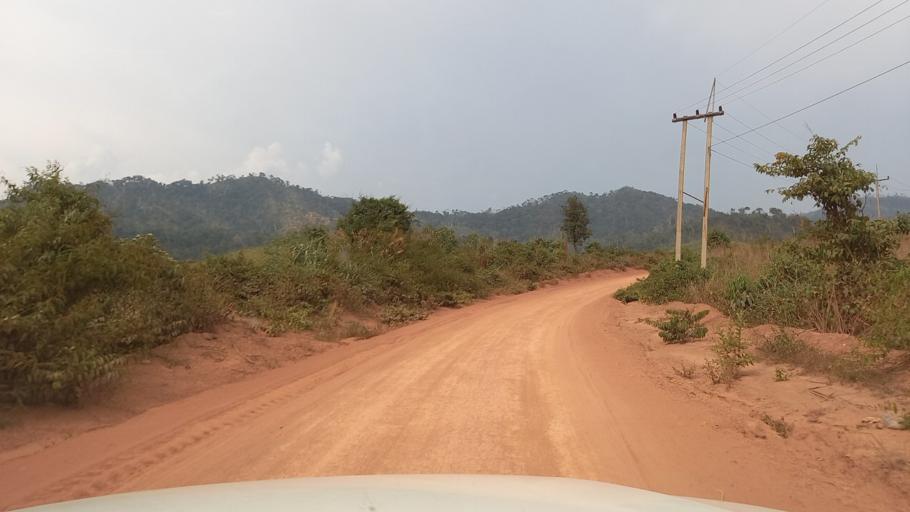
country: LA
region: Bolikhamxai
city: Bolikhan
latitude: 18.5366
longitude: 103.8090
